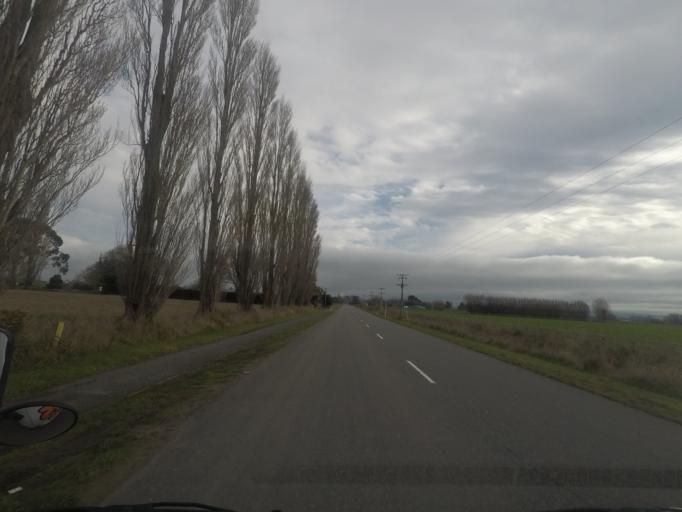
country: NZ
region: Canterbury
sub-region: Waimakariri District
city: Woodend
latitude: -43.2905
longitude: 172.6983
